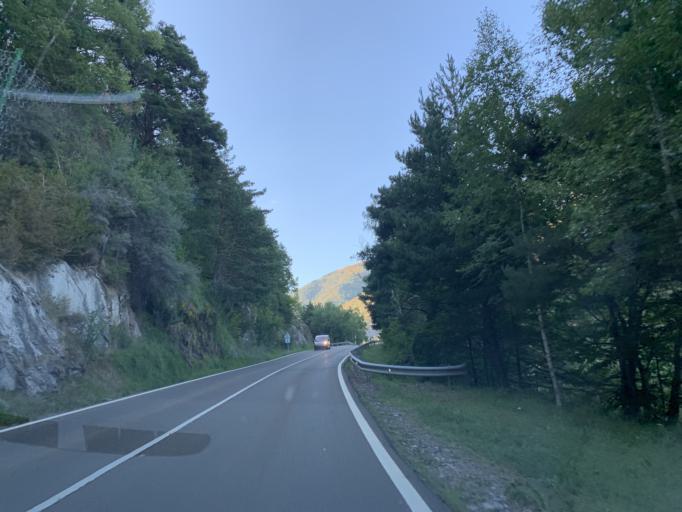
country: ES
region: Aragon
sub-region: Provincia de Huesca
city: Sallent de Gallego
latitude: 42.7442
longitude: -0.3156
